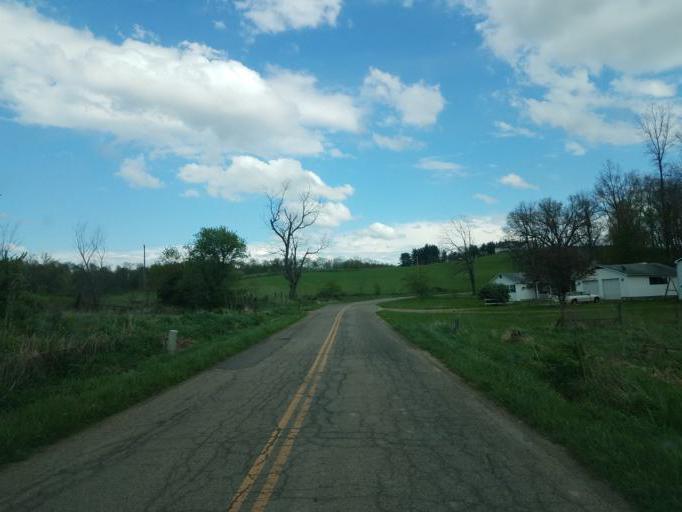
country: US
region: Ohio
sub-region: Knox County
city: Danville
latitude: 40.4800
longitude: -82.3465
